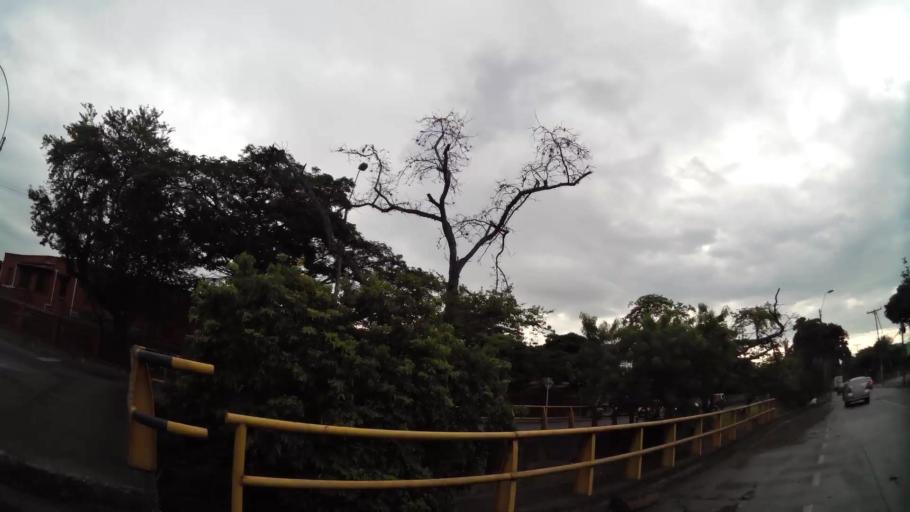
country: CO
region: Valle del Cauca
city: Cali
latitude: 3.4872
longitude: -76.5193
